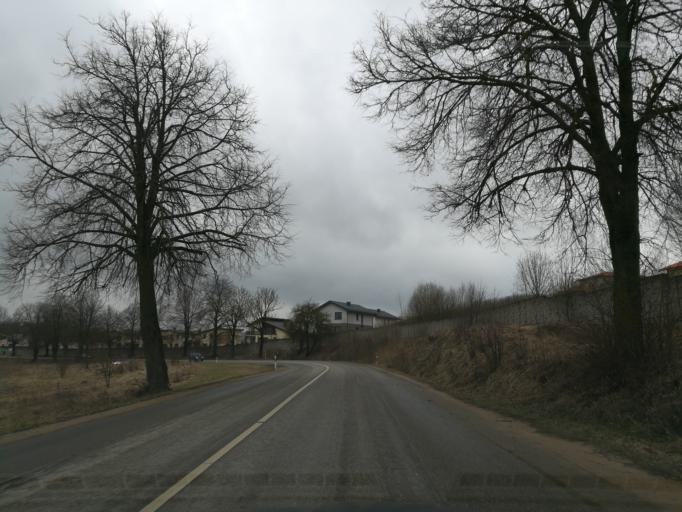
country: LT
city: Grigiskes
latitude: 54.6453
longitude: 25.0946
